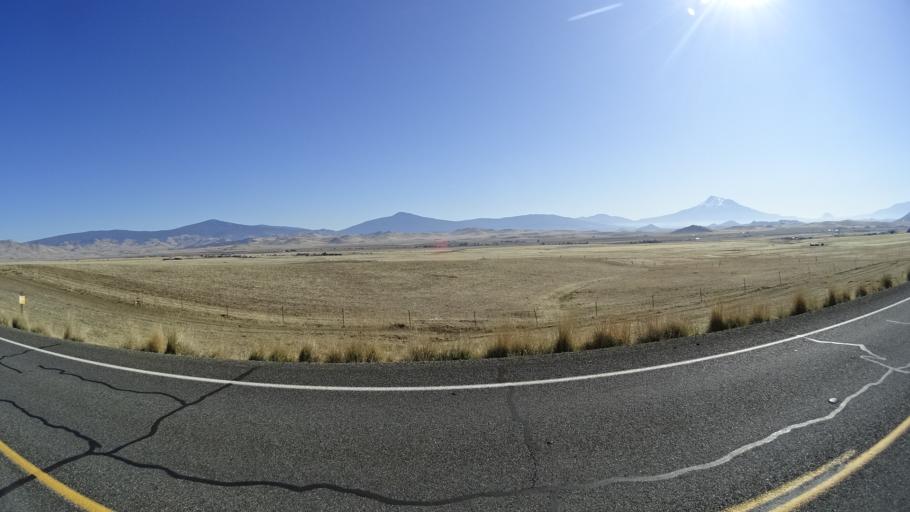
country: US
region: California
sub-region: Siskiyou County
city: Montague
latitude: 41.7827
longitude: -122.5196
